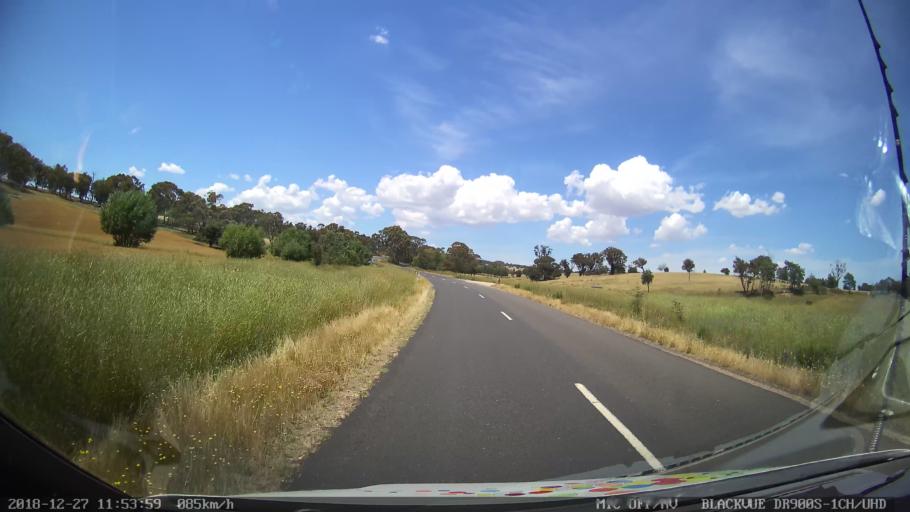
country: AU
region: New South Wales
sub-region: Blayney
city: Blayney
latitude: -33.6692
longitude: 149.4019
